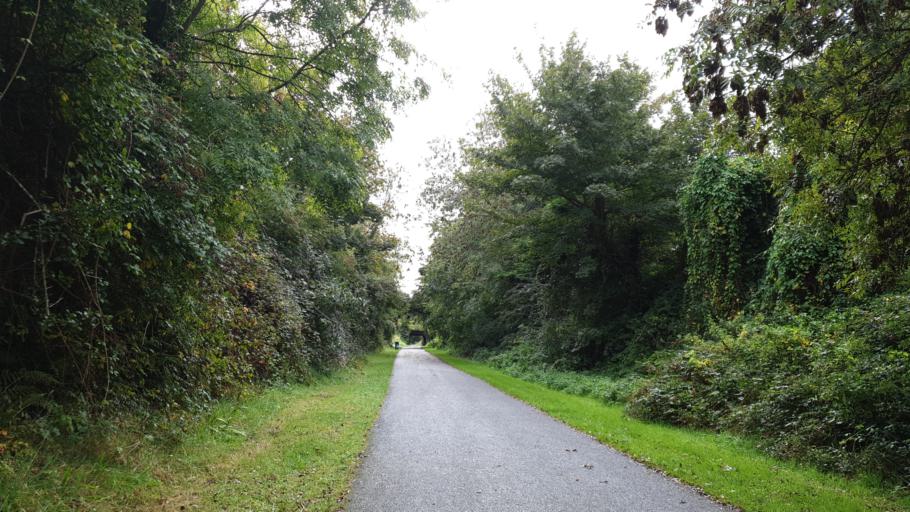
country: IE
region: Munster
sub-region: County Cork
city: Cork
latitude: 51.8916
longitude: -8.4132
